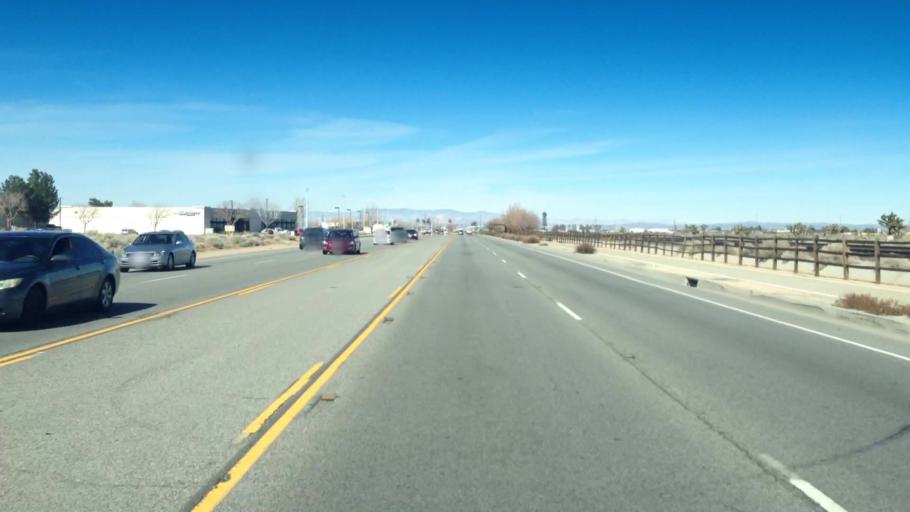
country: US
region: California
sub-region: Los Angeles County
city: Desert View Highlands
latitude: 34.6374
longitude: -118.1269
